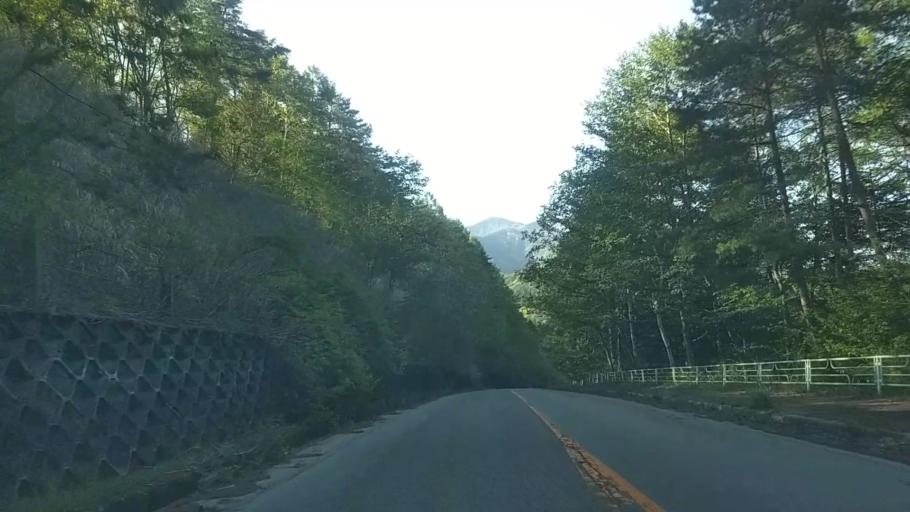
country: JP
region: Yamanashi
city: Nirasaki
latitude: 35.9012
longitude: 138.3748
